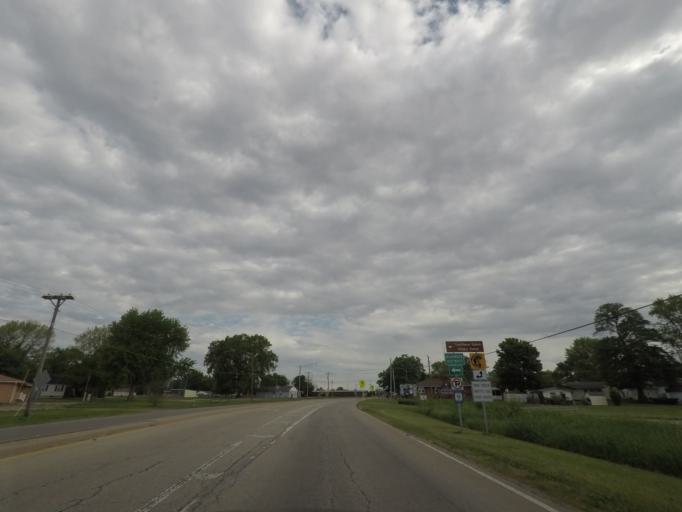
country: US
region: Illinois
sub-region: Logan County
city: Lincoln
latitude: 40.1370
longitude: -89.3487
